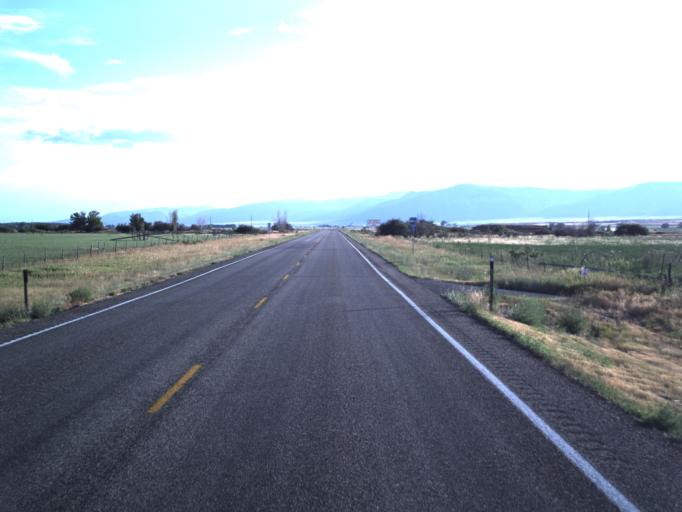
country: US
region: Utah
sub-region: Sanpete County
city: Mount Pleasant
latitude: 39.5166
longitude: -111.4876
